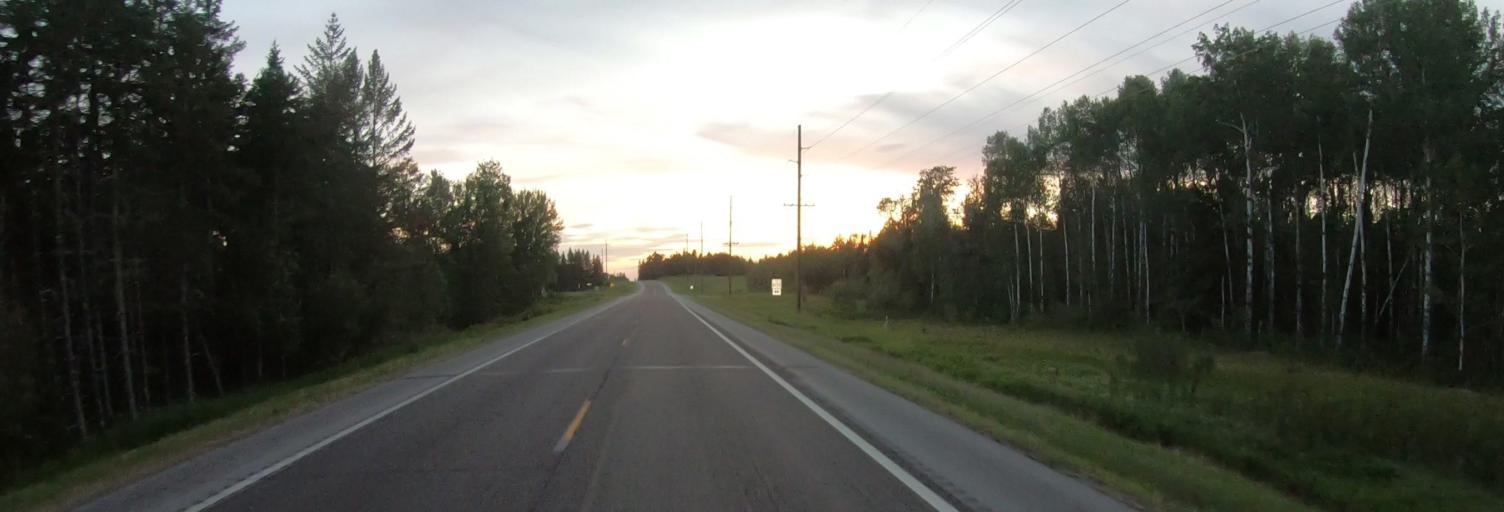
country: US
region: Minnesota
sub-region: Saint Louis County
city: Parkville
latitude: 47.8465
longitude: -92.5458
